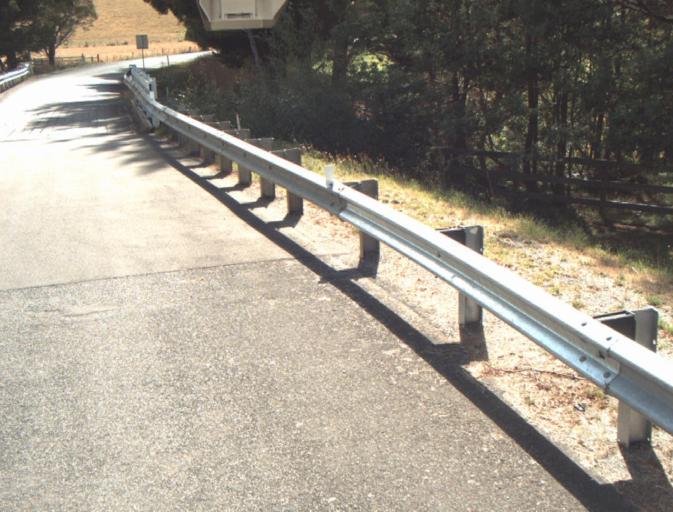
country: AU
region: Tasmania
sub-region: Launceston
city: Mayfield
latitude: -41.2604
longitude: 147.1609
